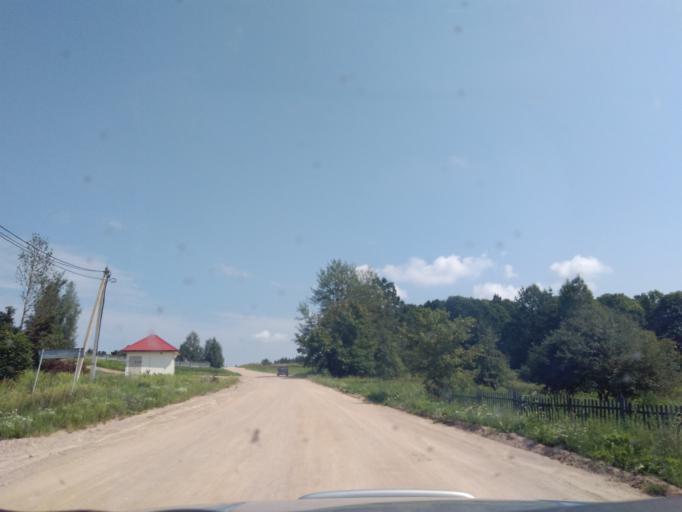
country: BY
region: Minsk
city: Khatsyezhyna
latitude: 53.8891
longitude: 27.2641
